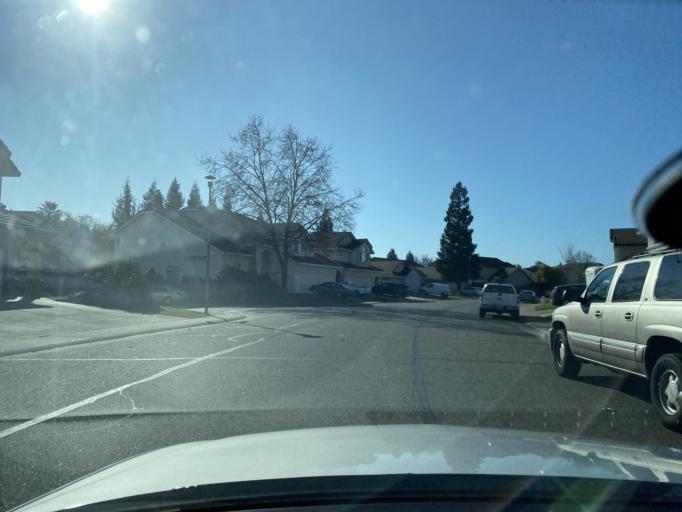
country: US
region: California
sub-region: Sacramento County
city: Elk Grove
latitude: 38.4335
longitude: -121.3838
